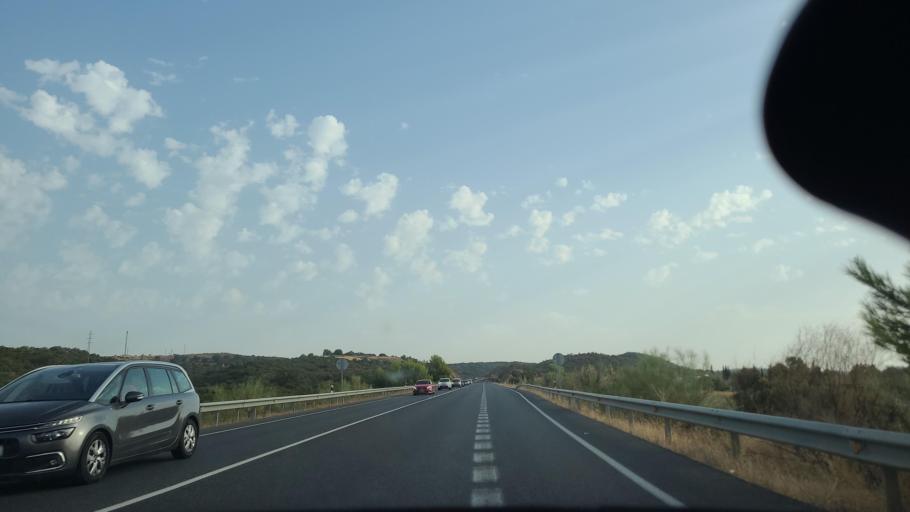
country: ES
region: Andalusia
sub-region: Province of Cordoba
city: Cordoba
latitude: 37.9326
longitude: -4.7655
